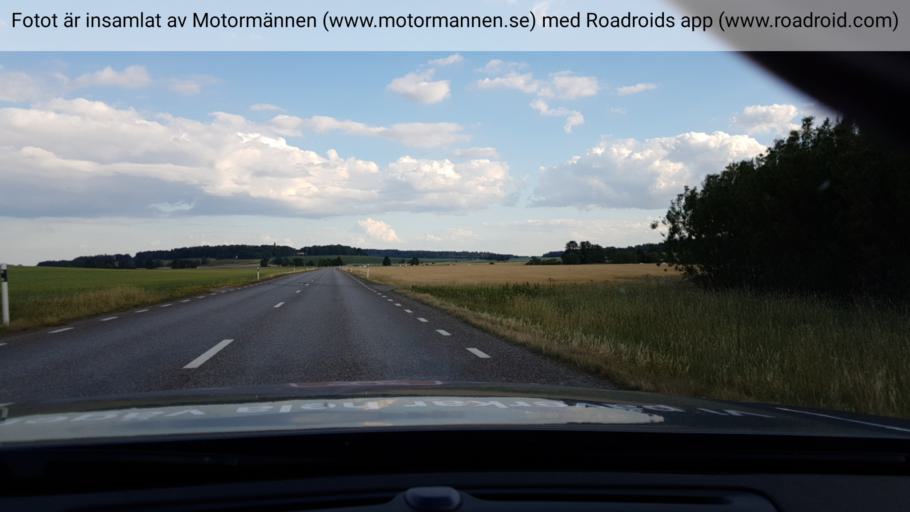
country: SE
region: Uppsala
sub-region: Heby Kommun
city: Morgongava
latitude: 59.8354
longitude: 16.9265
